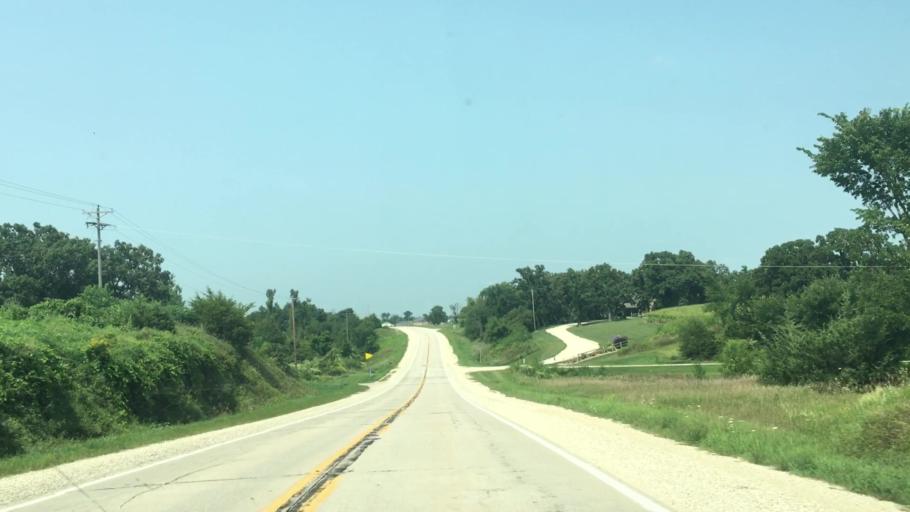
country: US
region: Iowa
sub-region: Fayette County
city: West Union
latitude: 43.1130
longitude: -91.8692
